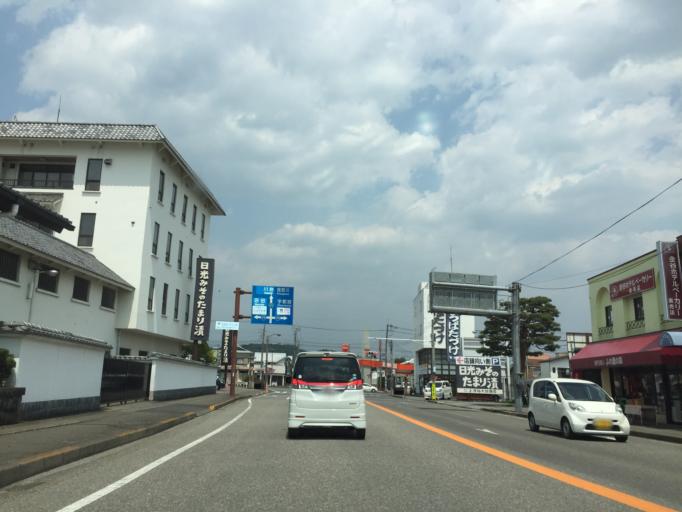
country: JP
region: Tochigi
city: Imaichi
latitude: 36.7245
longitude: 139.6843
